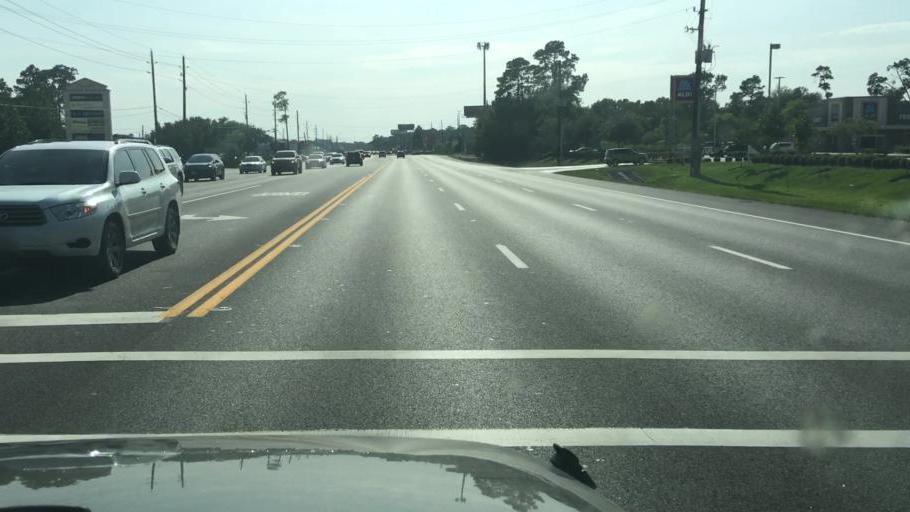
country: US
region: Texas
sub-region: Harris County
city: Humble
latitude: 30.0050
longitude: -95.2915
